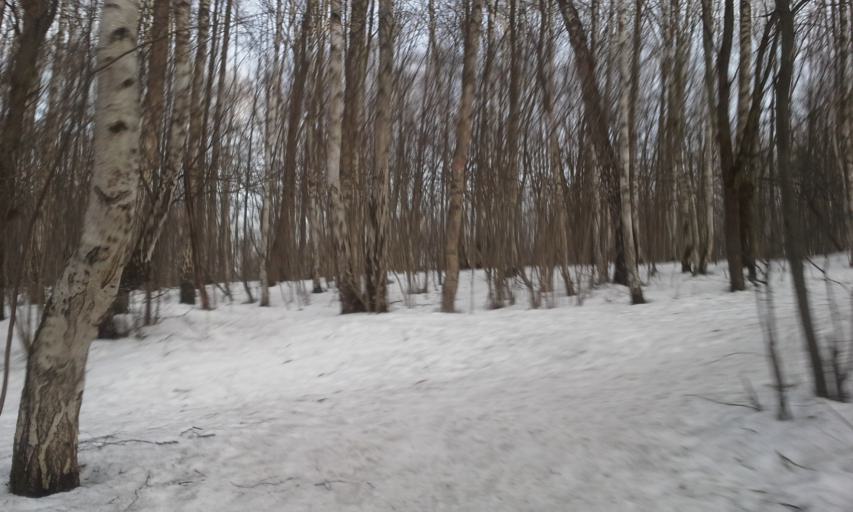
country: RU
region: Moscow
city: Zyuzino
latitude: 55.6384
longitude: 37.5766
